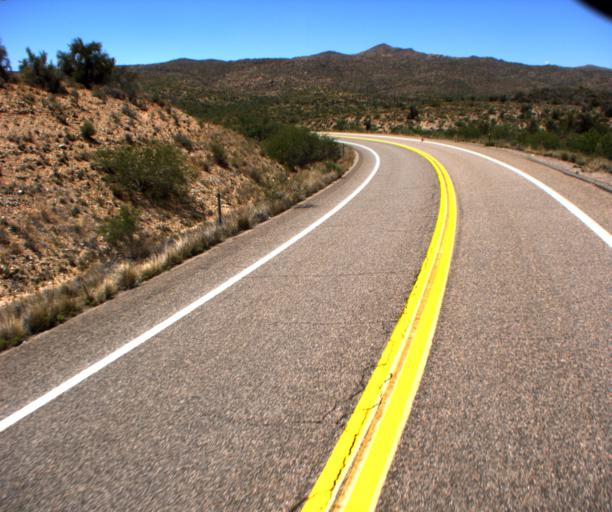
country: US
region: Arizona
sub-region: Yavapai County
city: Bagdad
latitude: 34.5162
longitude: -113.0756
